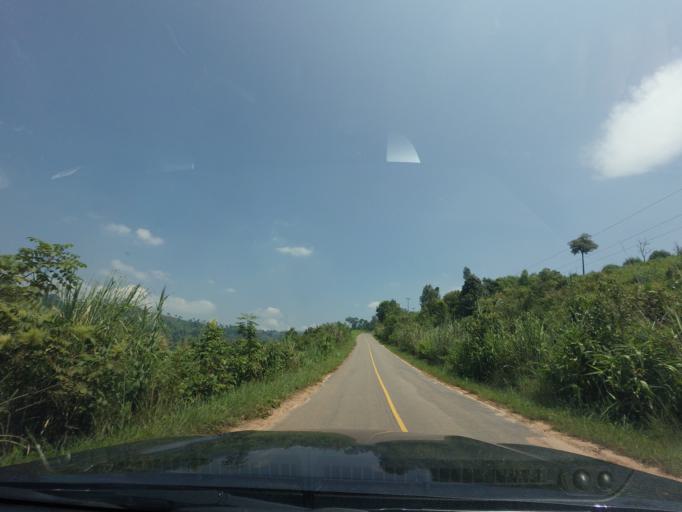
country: TH
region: Loei
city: Na Haeo
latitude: 17.5674
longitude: 100.8916
